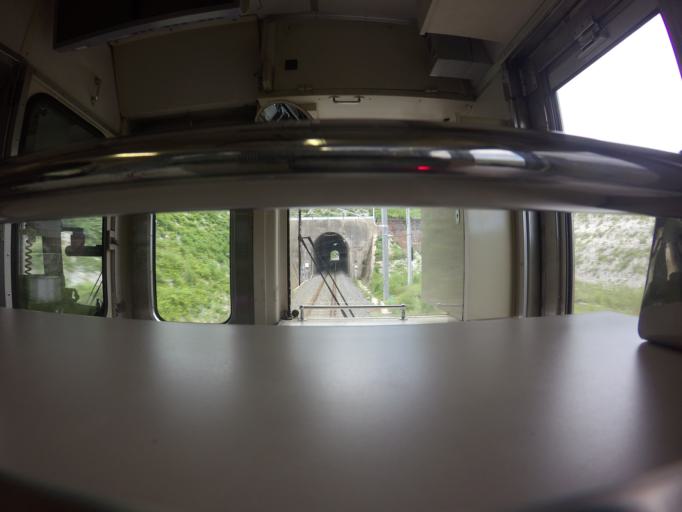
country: JP
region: Fukushima
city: Namie
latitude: 37.5151
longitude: 140.9741
